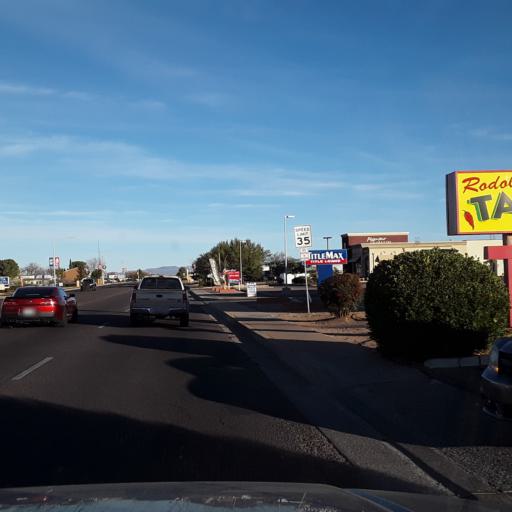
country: US
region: Arizona
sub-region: Cochise County
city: Sierra Vista
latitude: 31.5545
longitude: -110.2911
